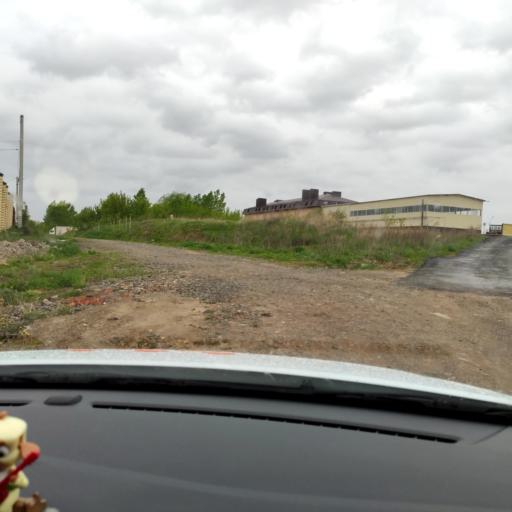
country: RU
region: Tatarstan
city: Stolbishchi
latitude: 55.7494
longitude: 49.2766
